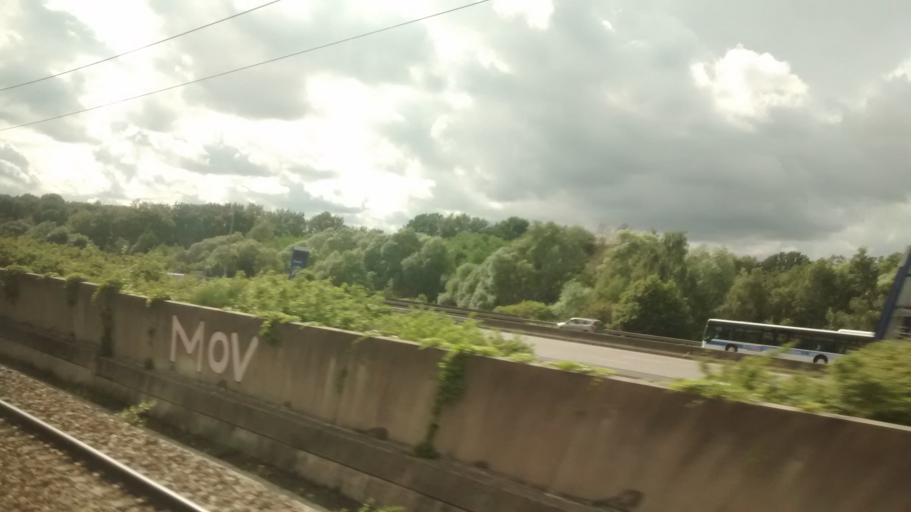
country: FR
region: Ile-de-France
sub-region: Departement de l'Essonne
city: Angervilliers
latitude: 48.6021
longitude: 2.0705
